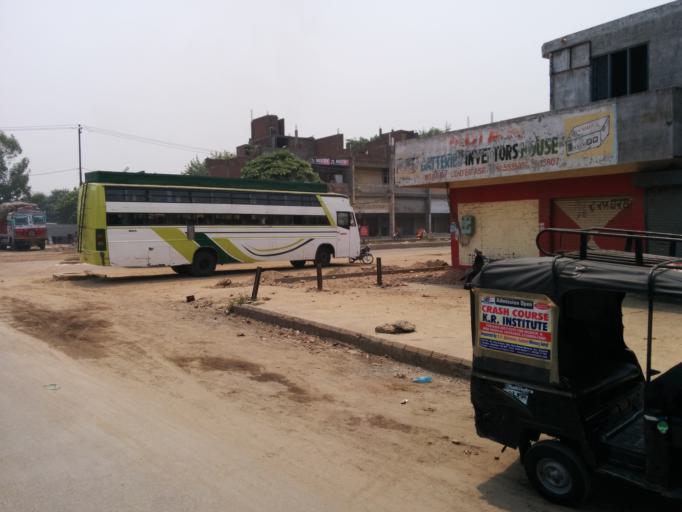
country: IN
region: Punjab
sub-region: Amritsar
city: Amritsar
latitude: 31.6277
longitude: 74.8876
